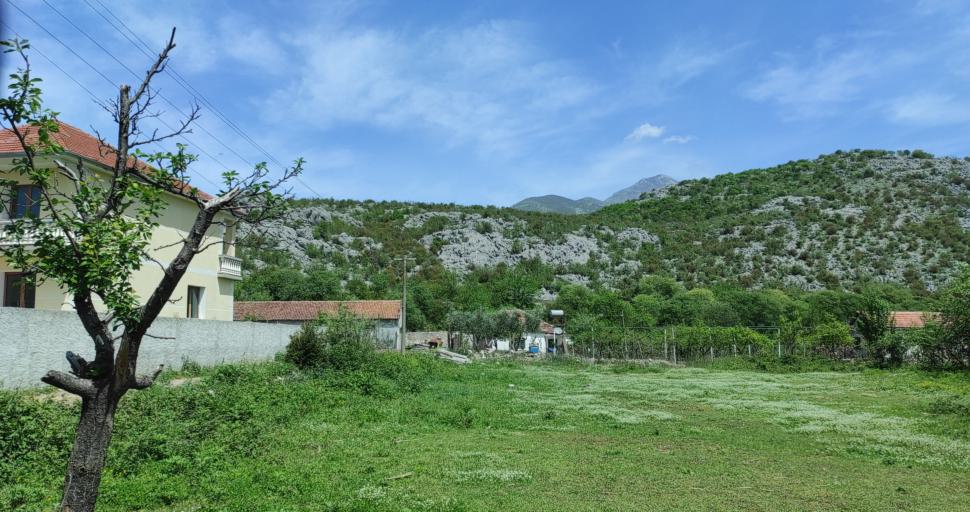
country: AL
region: Shkoder
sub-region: Rrethi i Malesia e Madhe
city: Gruemire
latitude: 42.1465
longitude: 19.5436
